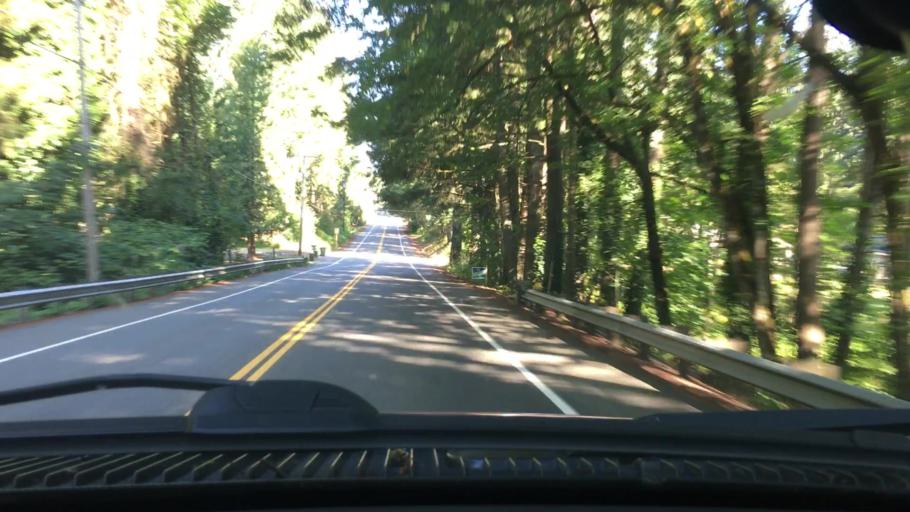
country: US
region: Washington
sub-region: King County
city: Covington
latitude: 47.3371
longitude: -122.1249
